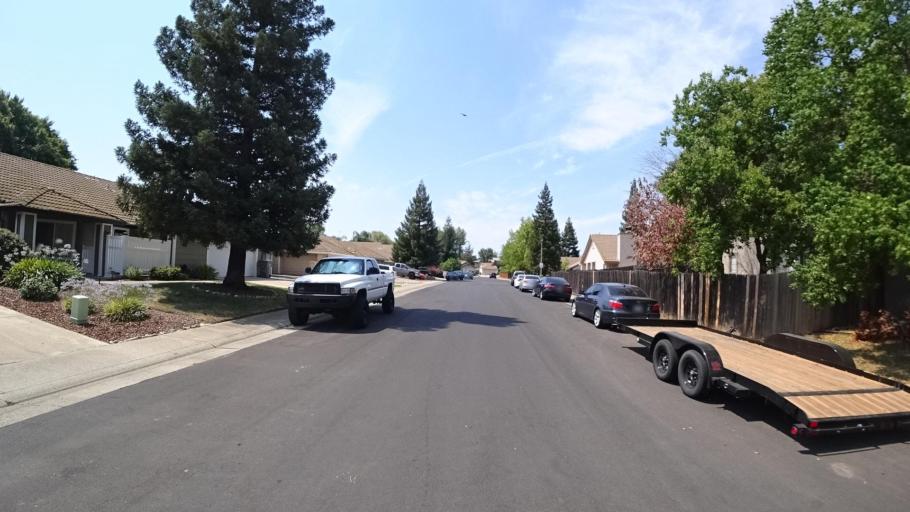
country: US
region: California
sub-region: Placer County
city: Rocklin
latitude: 38.7850
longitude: -121.2433
